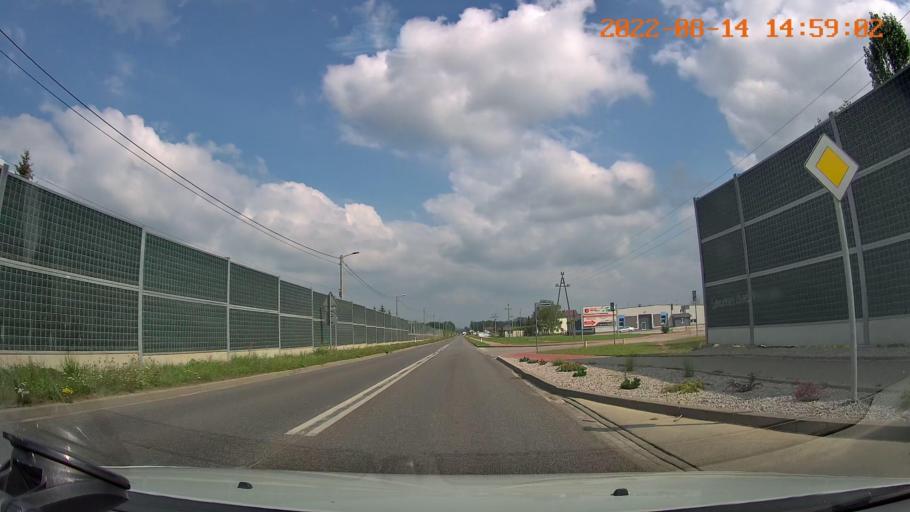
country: PL
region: Swietokrzyskie
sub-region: Powiat kielecki
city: Piekoszow
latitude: 50.8820
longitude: 20.4778
